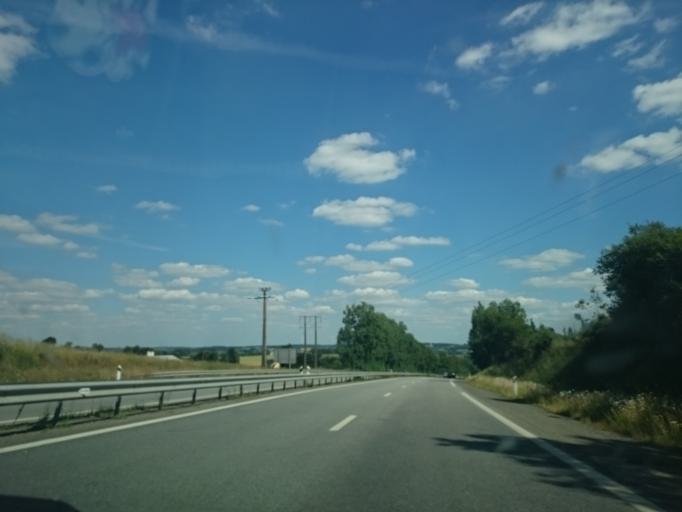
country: FR
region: Brittany
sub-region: Departement des Cotes-d'Armor
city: Saint-Barnabe
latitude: 48.1790
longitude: -2.6626
